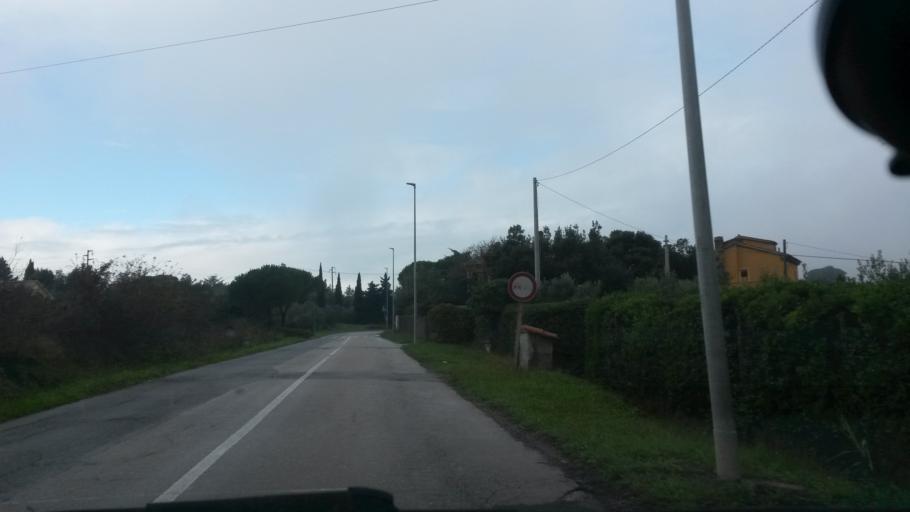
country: IT
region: Tuscany
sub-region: Provincia di Livorno
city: Rosignano Marittimo
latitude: 43.4172
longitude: 10.4616
